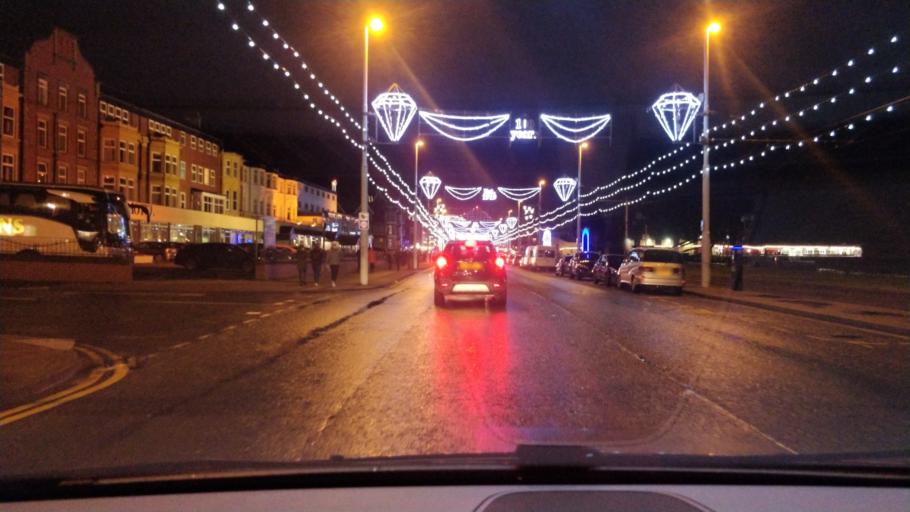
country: GB
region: England
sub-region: Blackpool
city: Blackpool
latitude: 53.7977
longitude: -3.0559
